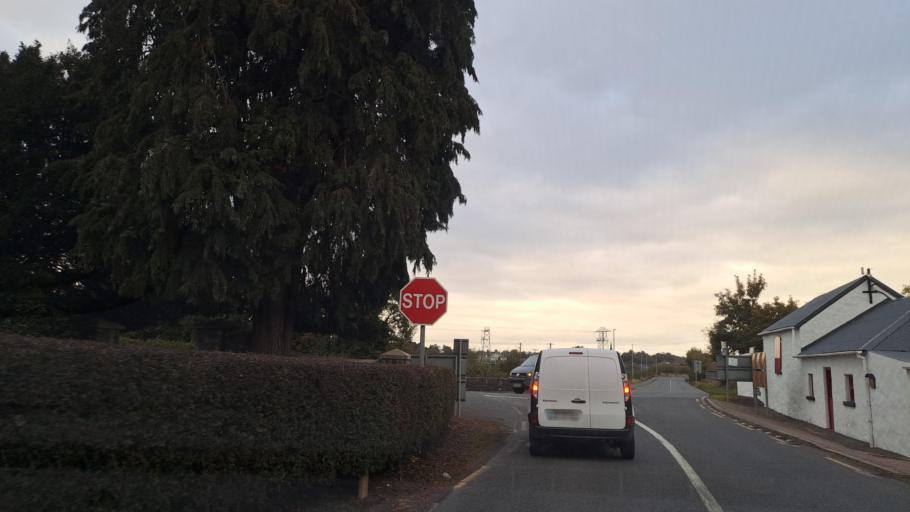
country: IE
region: Ulster
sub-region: County Monaghan
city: Monaghan
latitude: 54.1195
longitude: -6.9084
